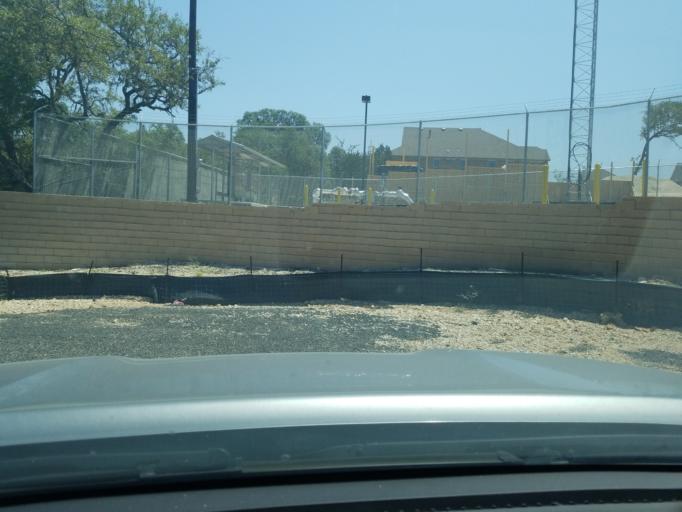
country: US
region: Texas
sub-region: Bexar County
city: Timberwood Park
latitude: 29.6844
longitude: -98.4808
